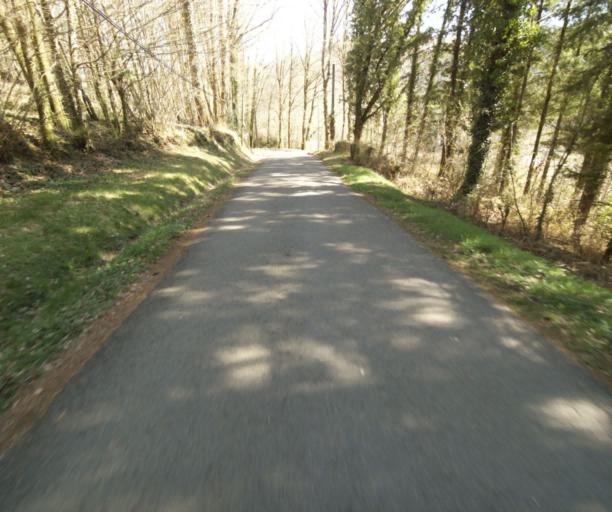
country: FR
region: Limousin
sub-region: Departement de la Correze
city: Tulle
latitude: 45.2735
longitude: 1.7281
